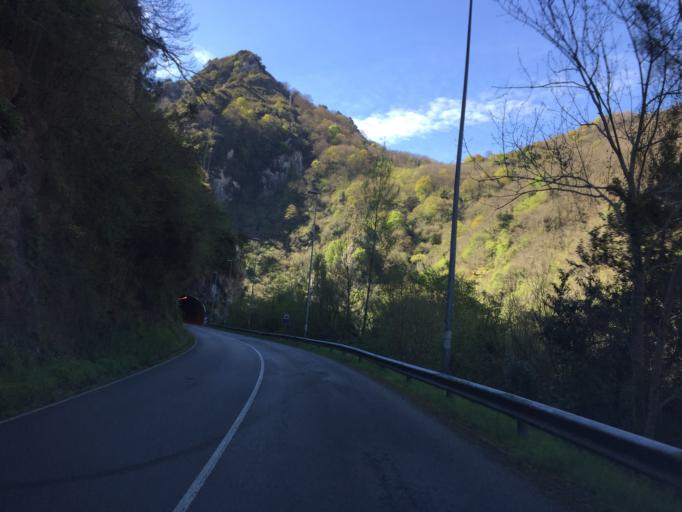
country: ES
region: Asturias
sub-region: Province of Asturias
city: Proaza
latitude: 43.3006
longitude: -5.9885
